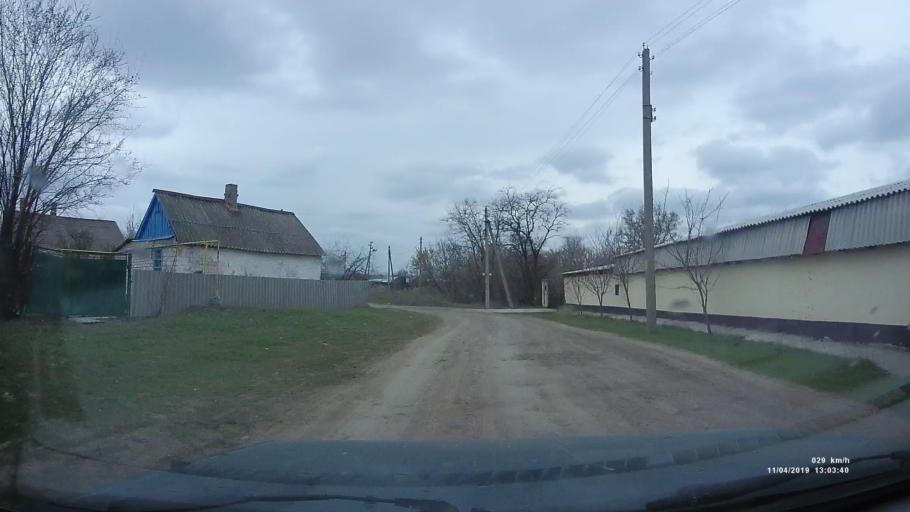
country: RU
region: Rostov
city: Staraya Stanitsa
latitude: 48.2872
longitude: 40.3498
